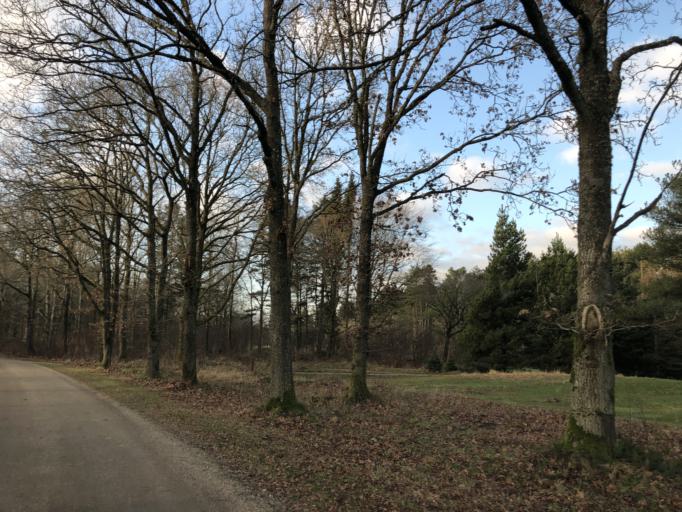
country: DK
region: Central Jutland
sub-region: Holstebro Kommune
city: Ulfborg
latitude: 56.3211
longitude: 8.4344
